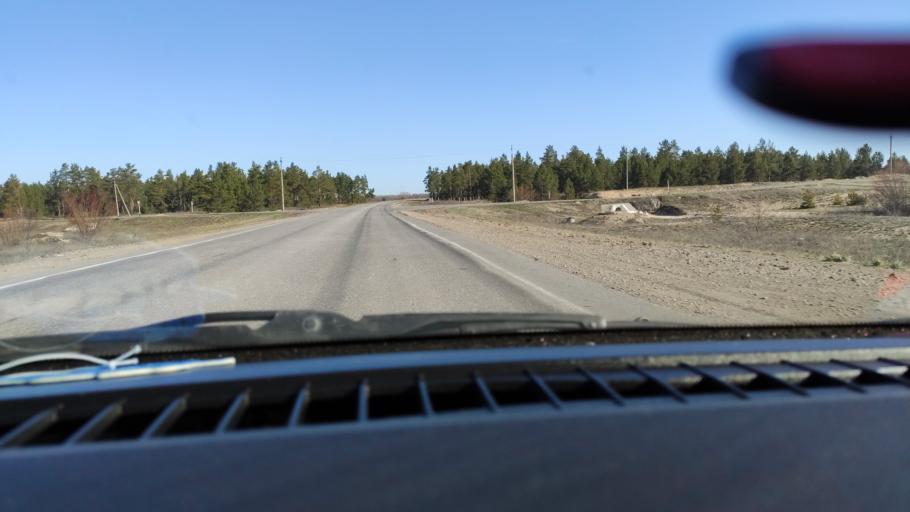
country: RU
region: Samara
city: Varlamovo
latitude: 53.1464
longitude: 48.2845
